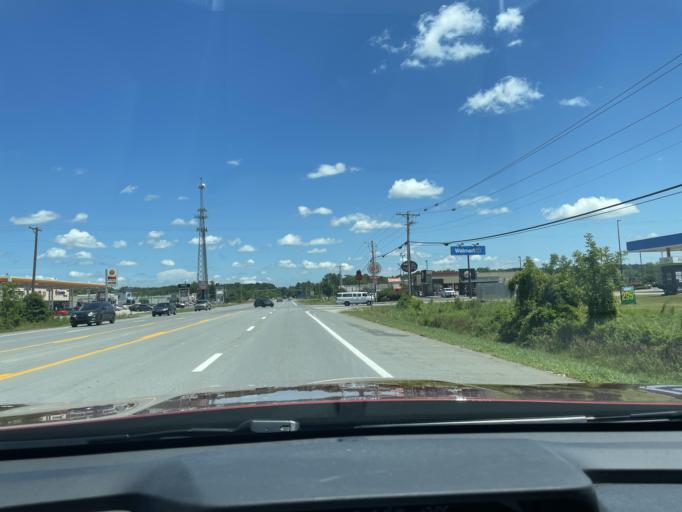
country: US
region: Arkansas
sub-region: Jefferson County
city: Pine Bluff
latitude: 34.1722
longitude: -92.0065
